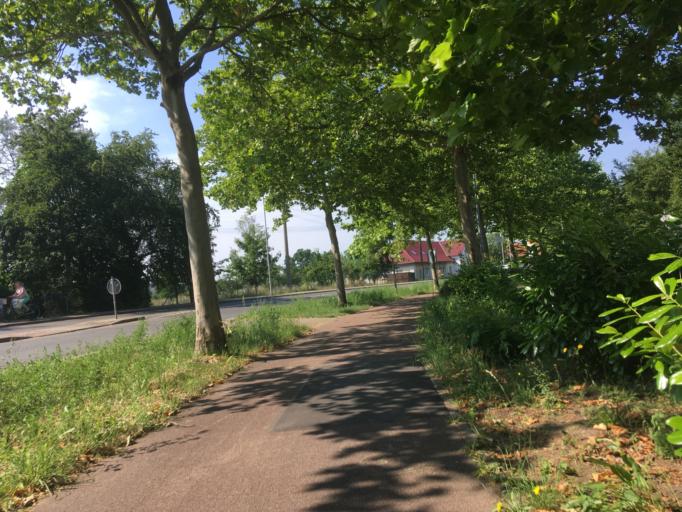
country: DE
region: Saxony-Anhalt
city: Dessau
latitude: 51.8142
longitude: 12.2238
